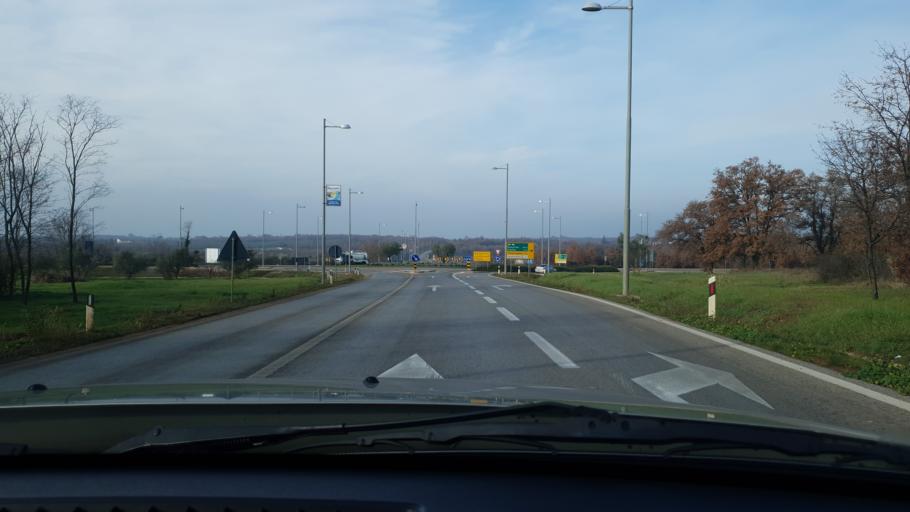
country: HR
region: Istarska
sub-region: Grad Porec
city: Porec
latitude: 45.2519
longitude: 13.6216
